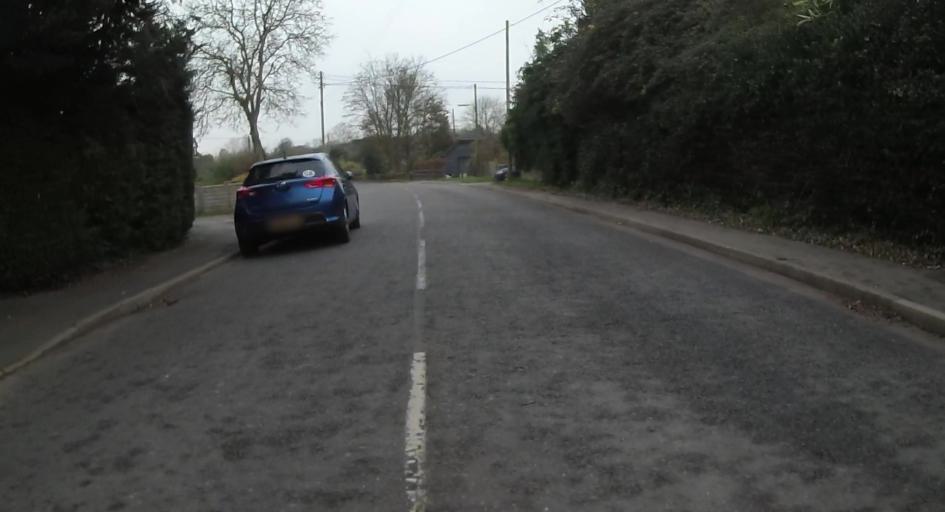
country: GB
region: England
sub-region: Hampshire
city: Kings Worthy
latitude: 51.1045
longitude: -1.3050
